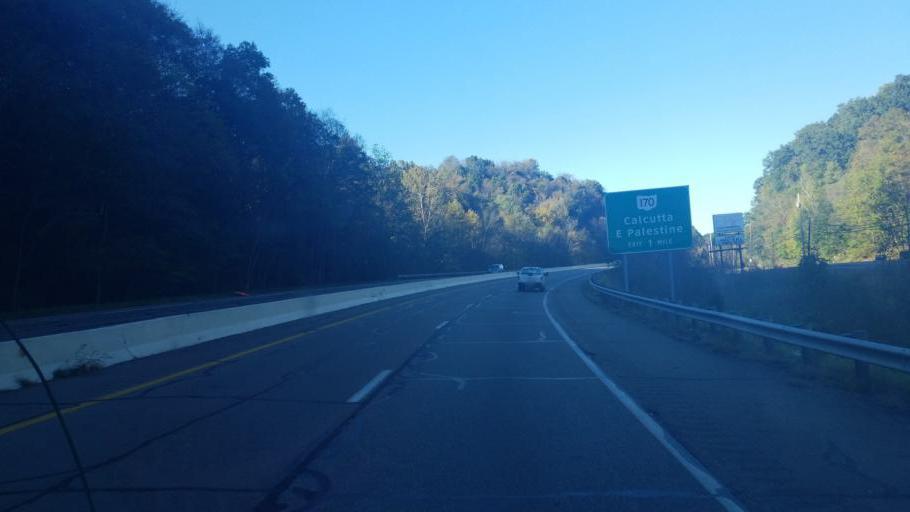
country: US
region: Ohio
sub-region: Columbiana County
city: La Croft
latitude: 40.6462
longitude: -80.5886
